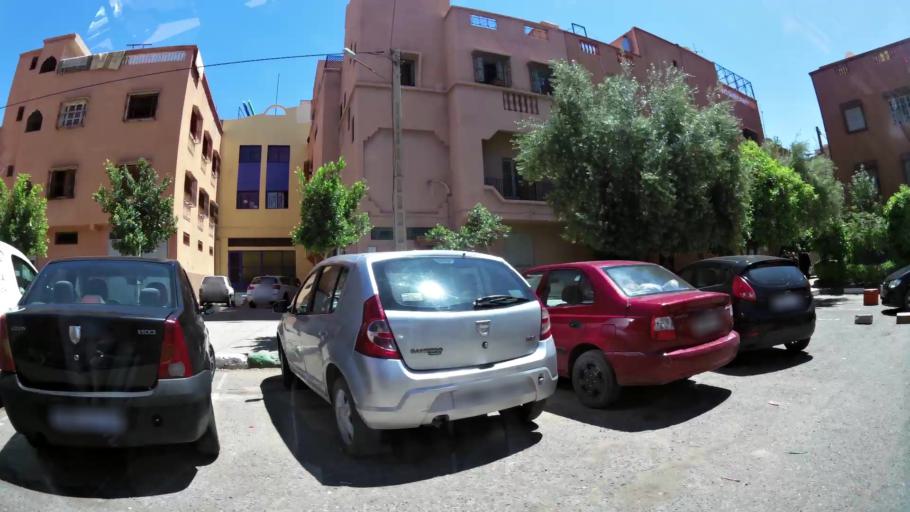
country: MA
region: Marrakech-Tensift-Al Haouz
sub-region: Marrakech
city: Marrakesh
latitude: 31.6364
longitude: -8.0575
